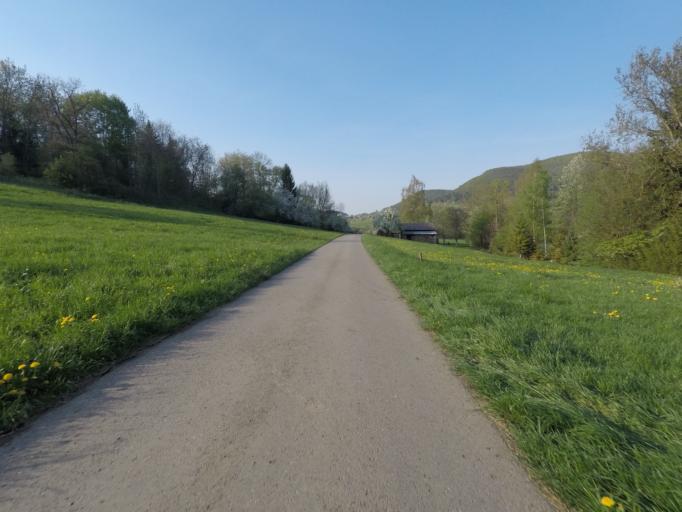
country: DE
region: Baden-Wuerttemberg
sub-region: Tuebingen Region
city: Eningen unter Achalm
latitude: 48.4671
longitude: 9.2602
